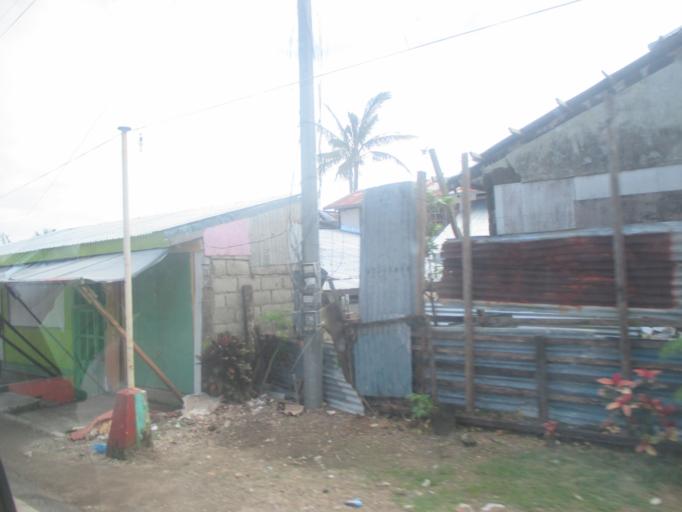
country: PH
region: Eastern Visayas
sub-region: Province of Eastern Samar
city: Salcedo
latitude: 11.1475
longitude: 125.6638
